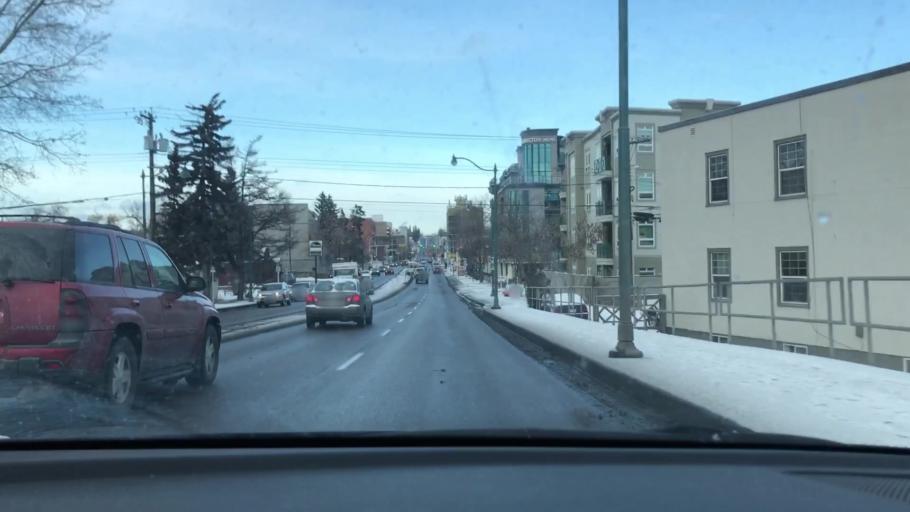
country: CA
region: Alberta
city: Calgary
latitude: 51.0502
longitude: -114.0946
